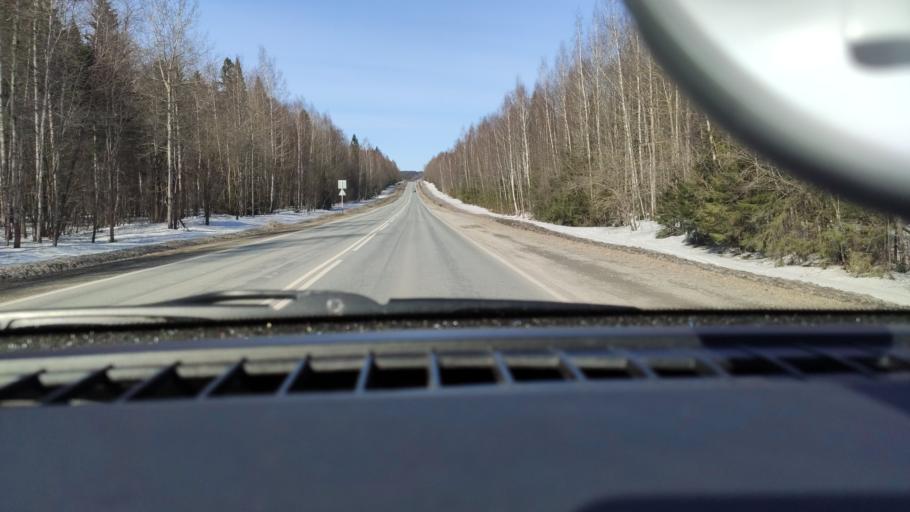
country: RU
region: Perm
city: Perm
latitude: 58.1465
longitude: 56.2617
